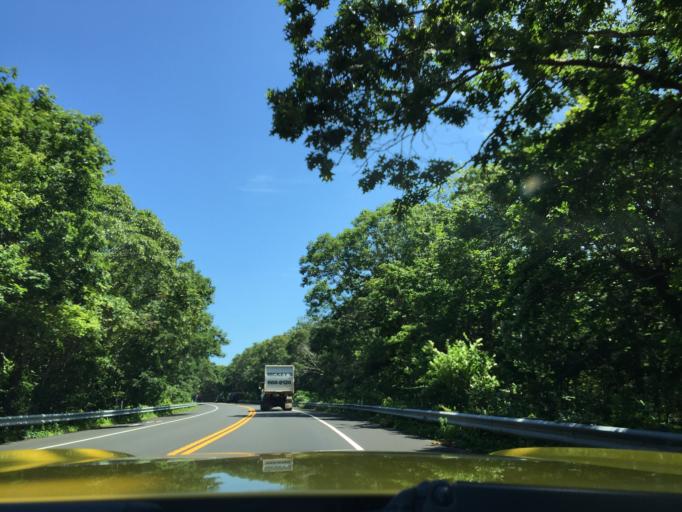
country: US
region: New York
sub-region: Suffolk County
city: Montauk
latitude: 41.0197
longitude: -71.9946
